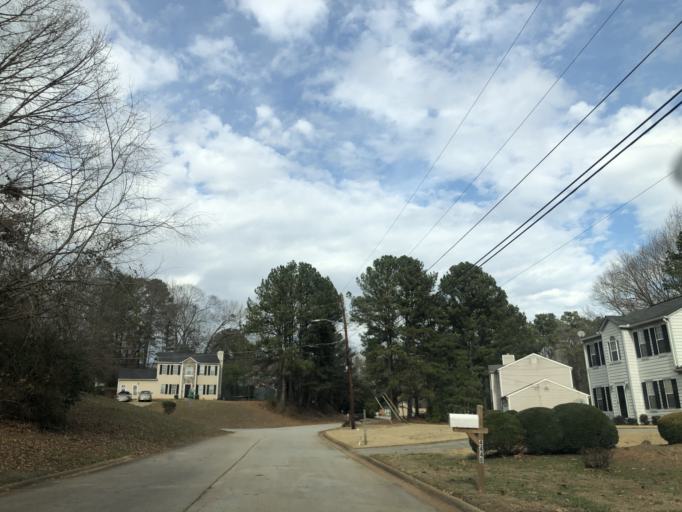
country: US
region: Georgia
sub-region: DeKalb County
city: Panthersville
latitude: 33.6723
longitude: -84.2101
